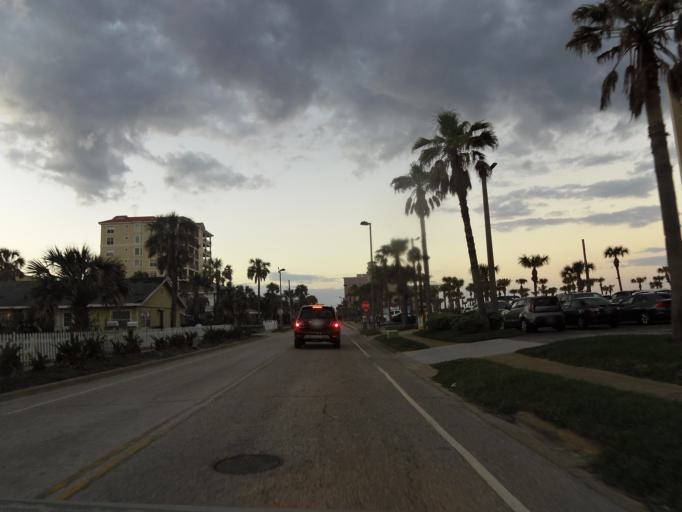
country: US
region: Florida
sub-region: Duval County
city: Jacksonville Beach
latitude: 30.2824
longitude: -81.3883
